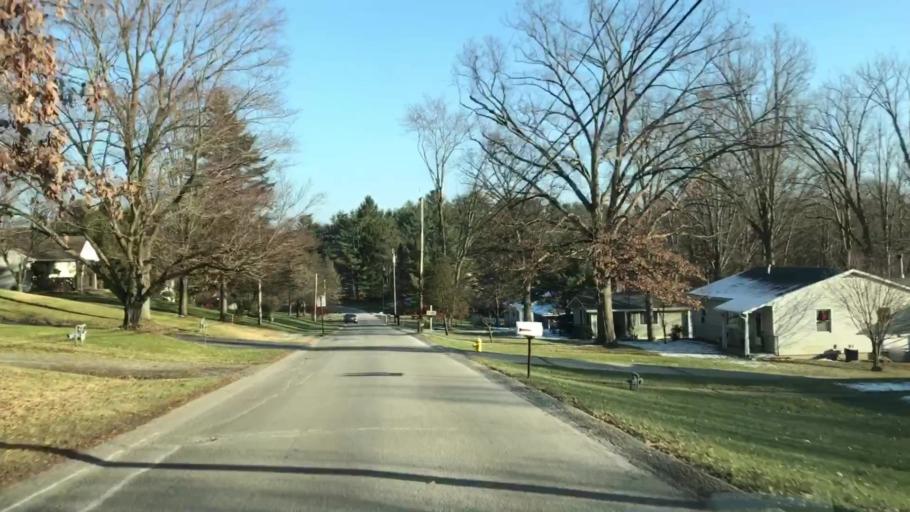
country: US
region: Pennsylvania
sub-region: Allegheny County
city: Gibsonia
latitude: 40.6101
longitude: -79.9739
